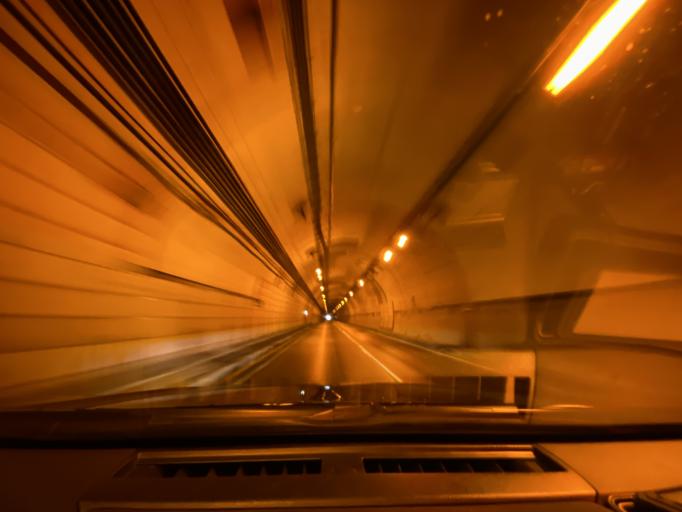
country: JP
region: Hokkaido
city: Rumoi
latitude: 43.7958
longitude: 141.3762
